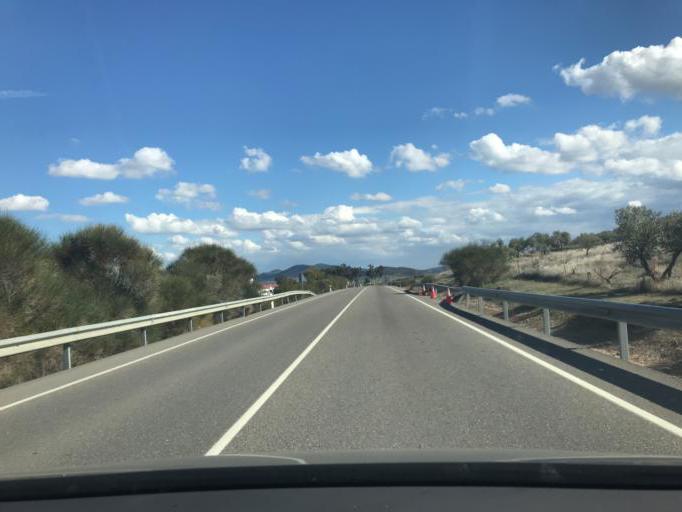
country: ES
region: Andalusia
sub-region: Province of Cordoba
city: Fuente Obejuna
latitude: 38.2757
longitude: -5.4166
